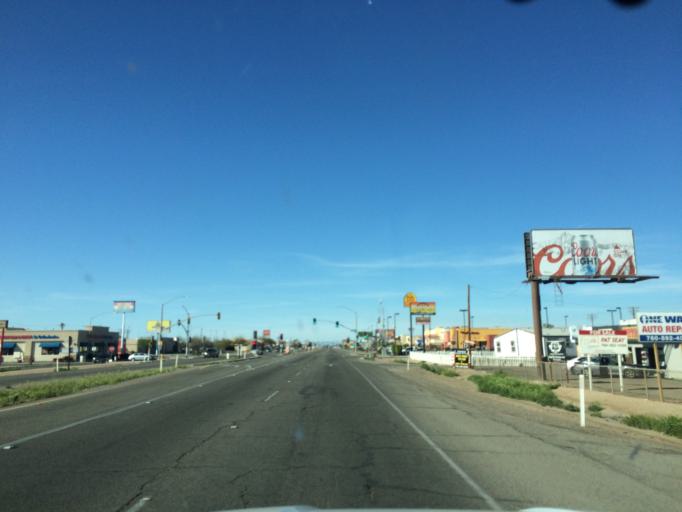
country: US
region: California
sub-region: Imperial County
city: El Centro
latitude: 32.8046
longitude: -115.5698
